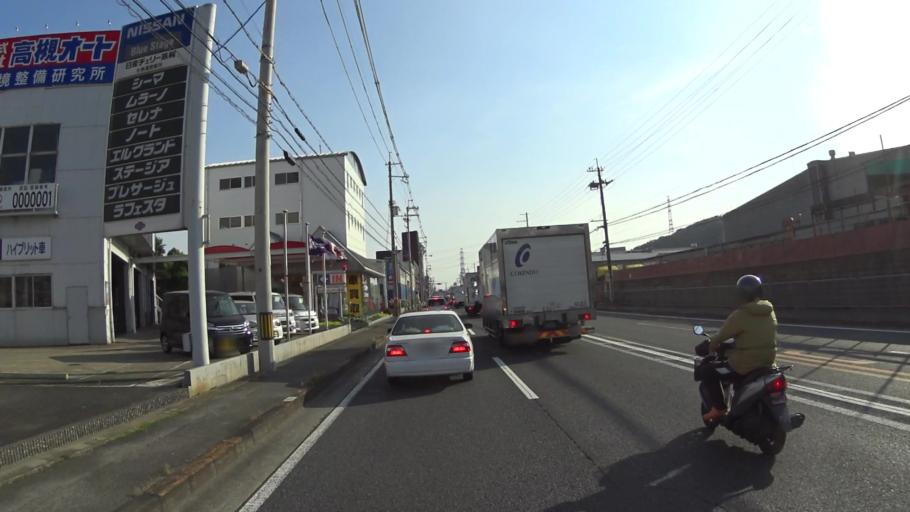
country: JP
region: Kyoto
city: Yawata
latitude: 34.8749
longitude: 135.6670
